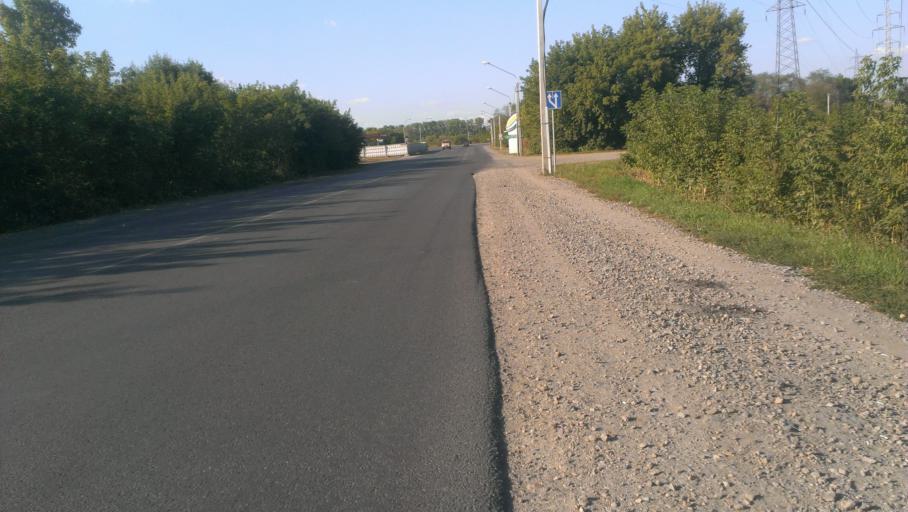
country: RU
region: Altai Krai
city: Novosilikatnyy
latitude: 53.3468
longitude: 83.6201
